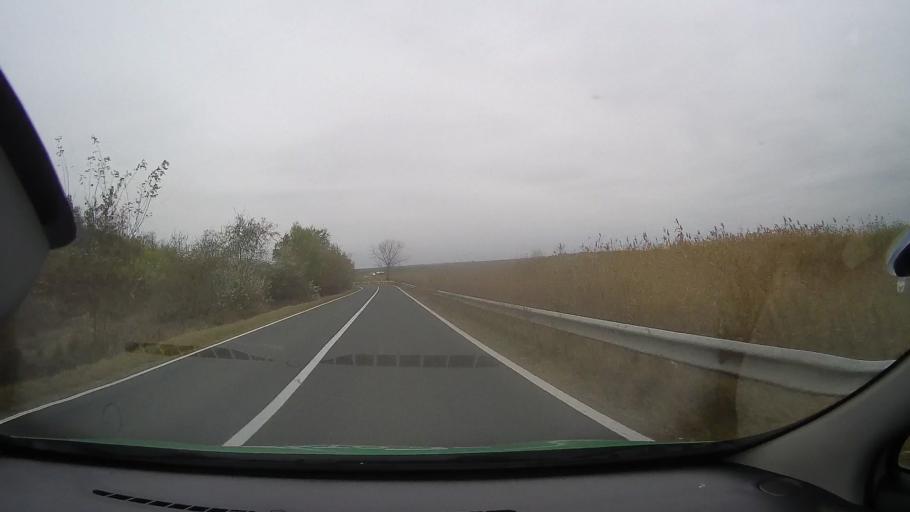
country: RO
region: Constanta
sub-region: Comuna Garliciu
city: Garliciu
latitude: 44.7076
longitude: 28.0648
